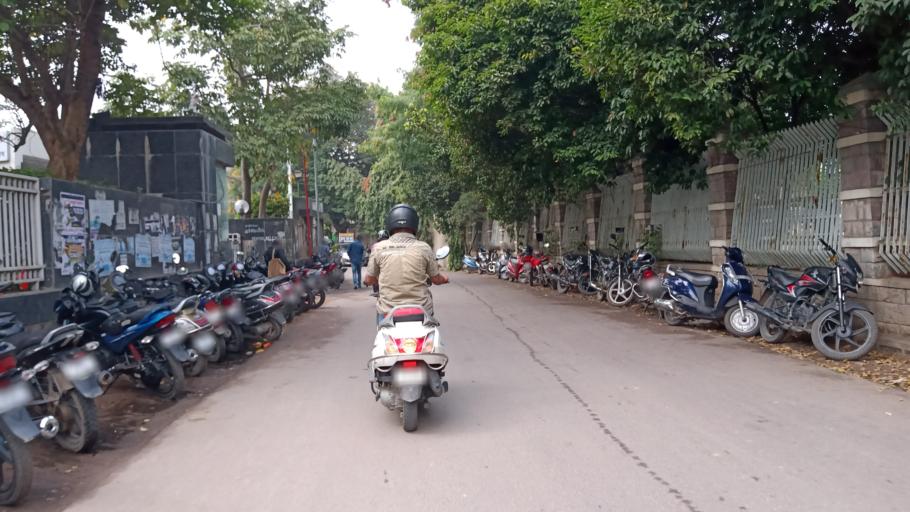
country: IN
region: Telangana
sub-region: Rangareddi
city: Kukatpalli
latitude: 17.4479
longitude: 78.4405
